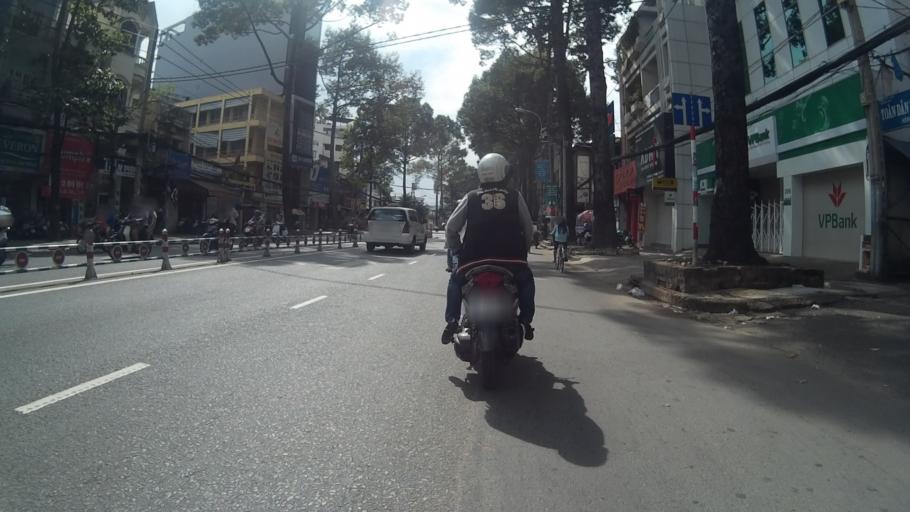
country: VN
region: Ho Chi Minh City
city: Quan Muoi
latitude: 10.7704
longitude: 106.6720
